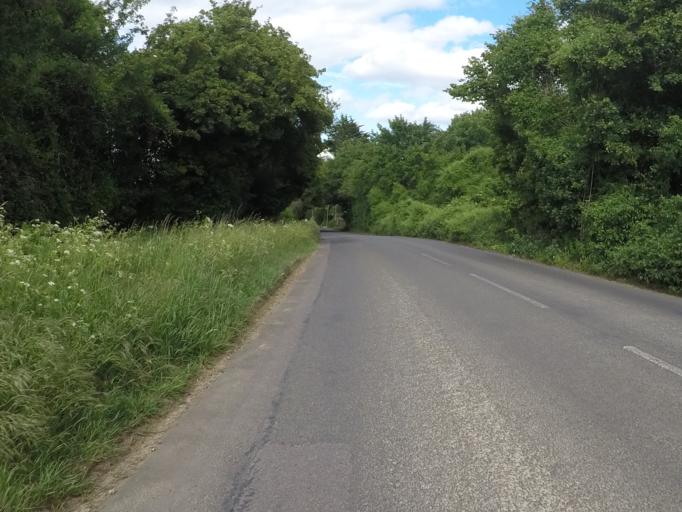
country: GB
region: England
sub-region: Oxfordshire
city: Charlbury
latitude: 51.8452
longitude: -1.4830
